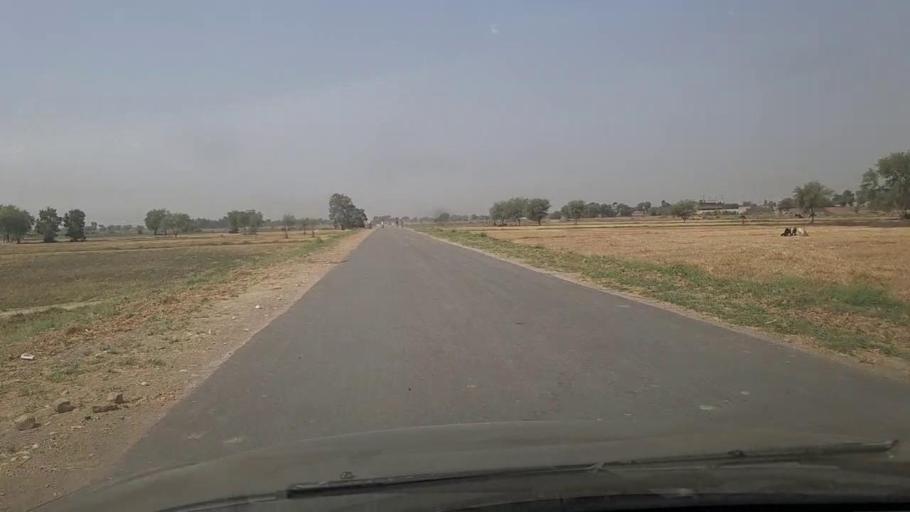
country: PK
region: Sindh
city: Khanpur
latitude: 27.9056
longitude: 69.5047
